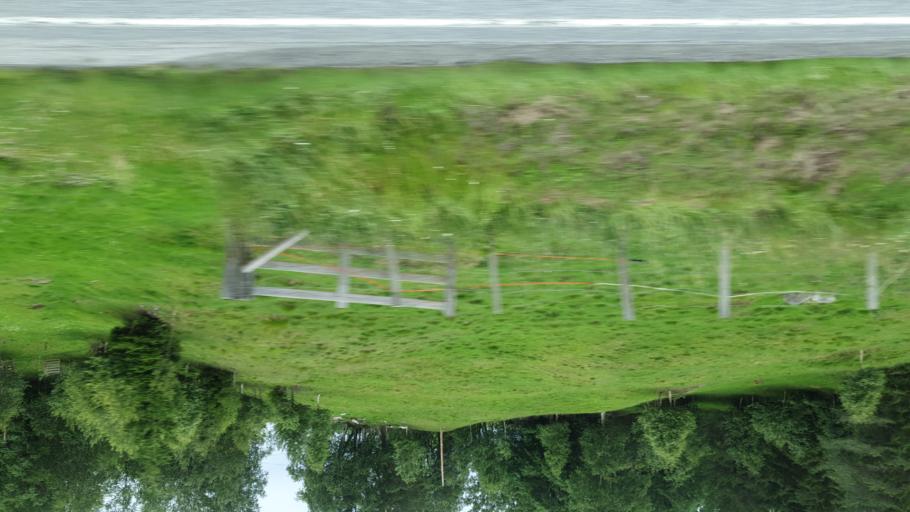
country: NO
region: Sor-Trondelag
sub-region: Rennebu
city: Berkak
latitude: 62.8793
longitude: 10.0908
